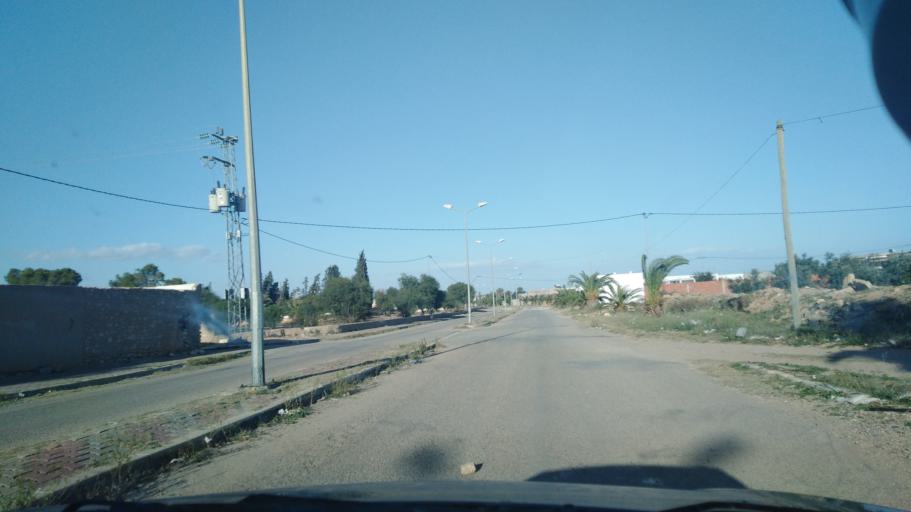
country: TN
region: Al Mahdiyah
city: Shurban
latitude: 34.9640
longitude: 10.3699
